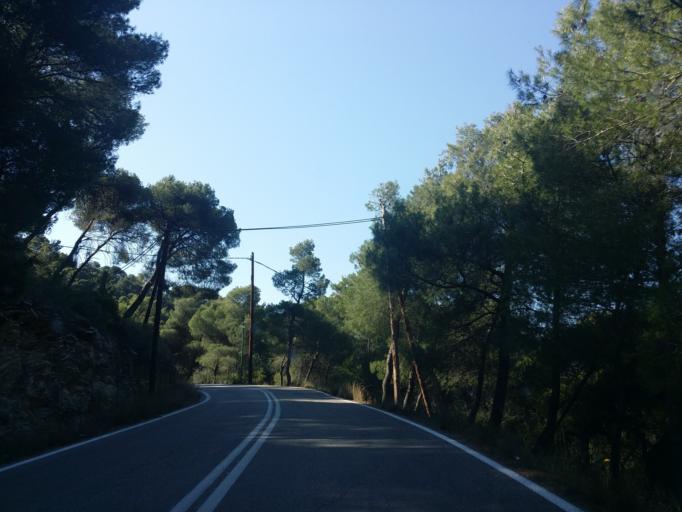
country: GR
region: Attica
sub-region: Nomos Piraios
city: Poros
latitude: 37.5144
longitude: 23.4608
